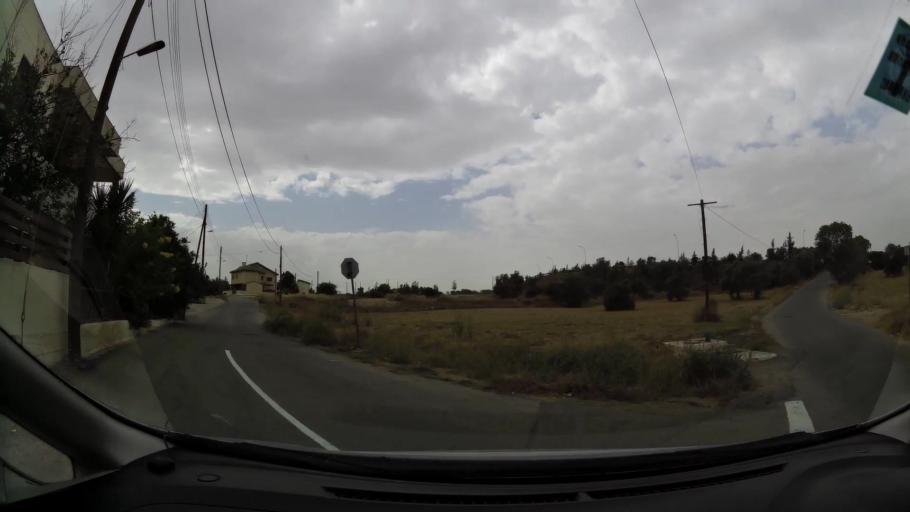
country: CY
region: Lefkosia
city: Geri
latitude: 35.1039
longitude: 33.3719
